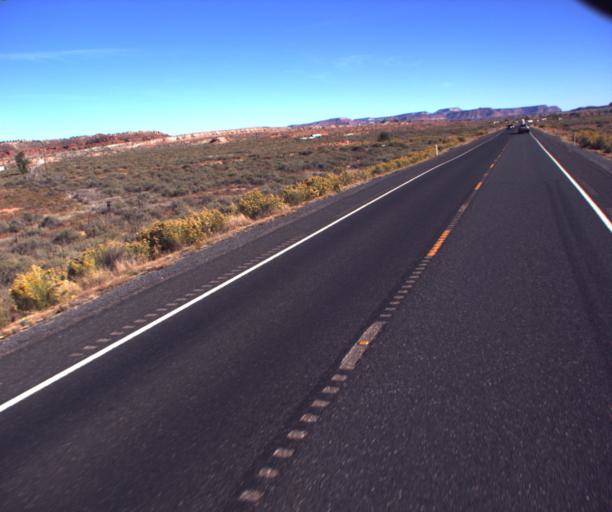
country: US
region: Arizona
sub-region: Coconino County
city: Fredonia
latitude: 36.9392
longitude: -112.5496
